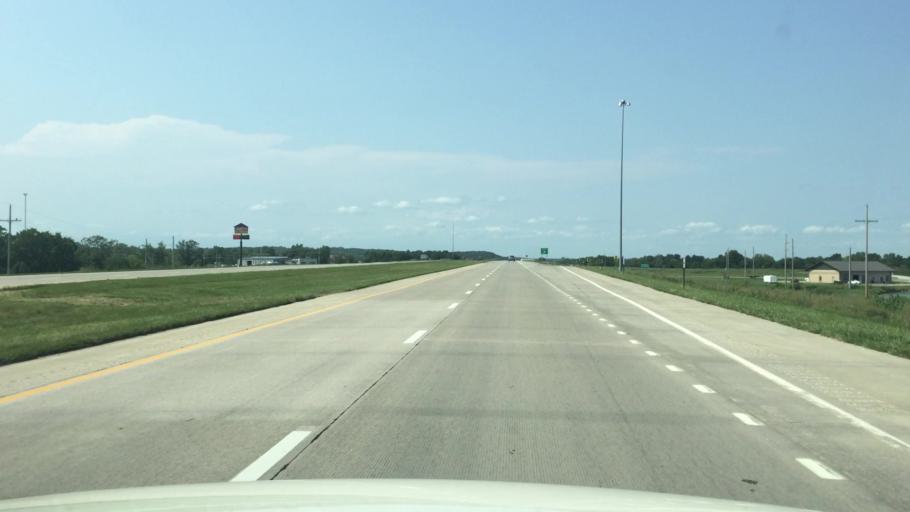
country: US
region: Kansas
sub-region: Linn County
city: Pleasanton
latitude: 38.1782
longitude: -94.6978
